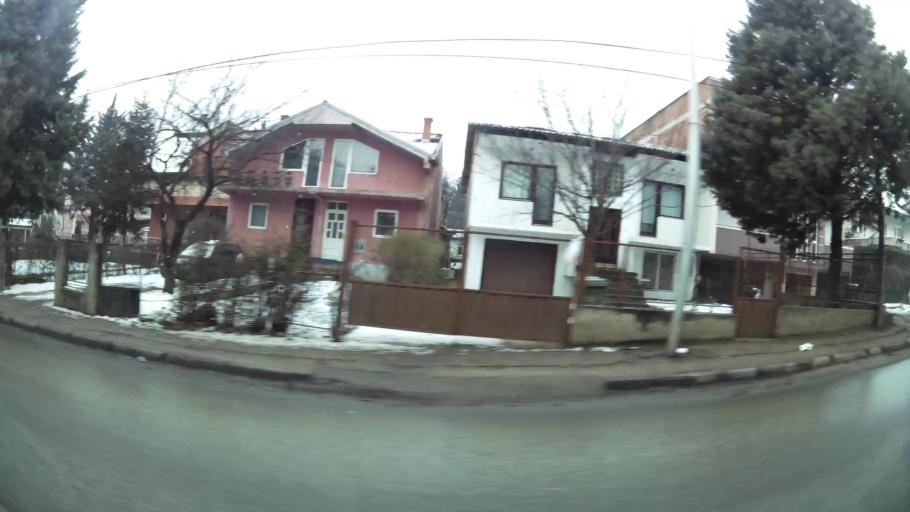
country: MK
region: Cair
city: Cair
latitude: 42.0184
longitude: 21.4526
